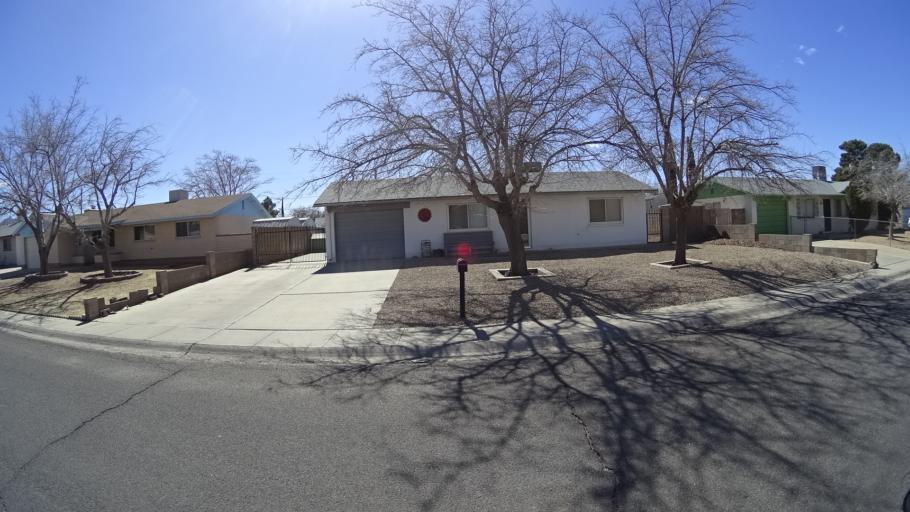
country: US
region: Arizona
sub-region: Mohave County
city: Kingman
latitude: 35.1958
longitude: -114.0191
